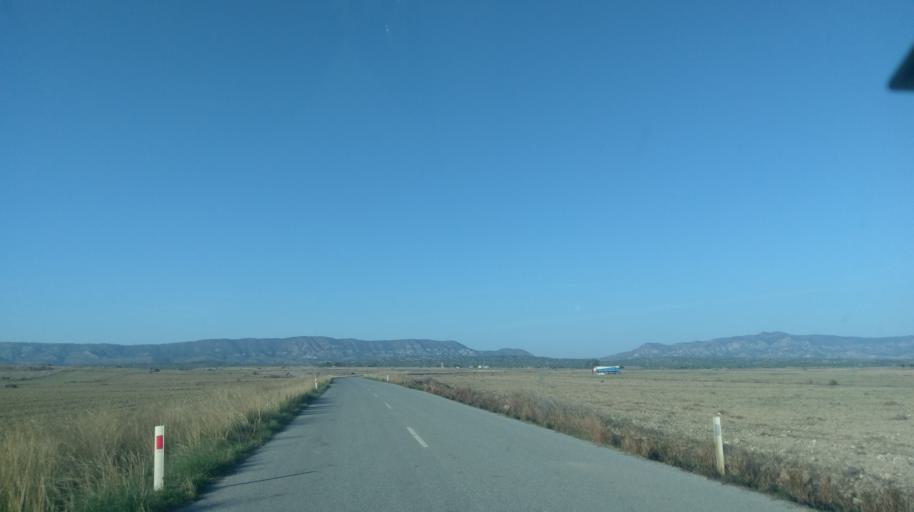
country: CY
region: Ammochostos
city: Lefkonoiko
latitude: 35.2649
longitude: 33.6867
